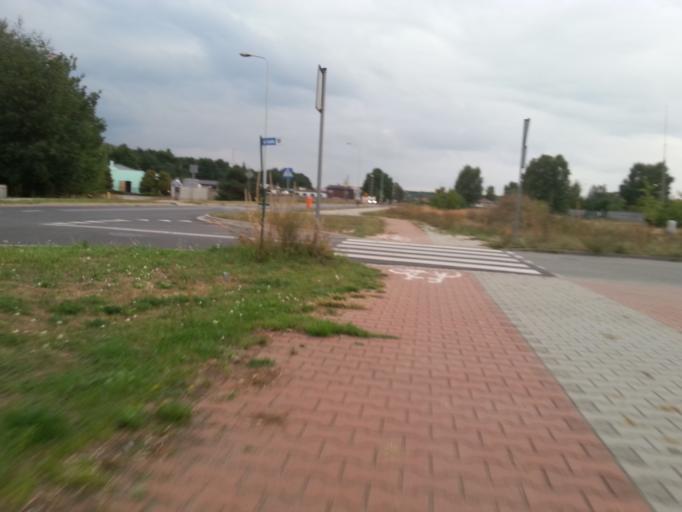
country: PL
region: Lower Silesian Voivodeship
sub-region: Powiat olesnicki
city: Twardogora
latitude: 51.3612
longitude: 17.4569
